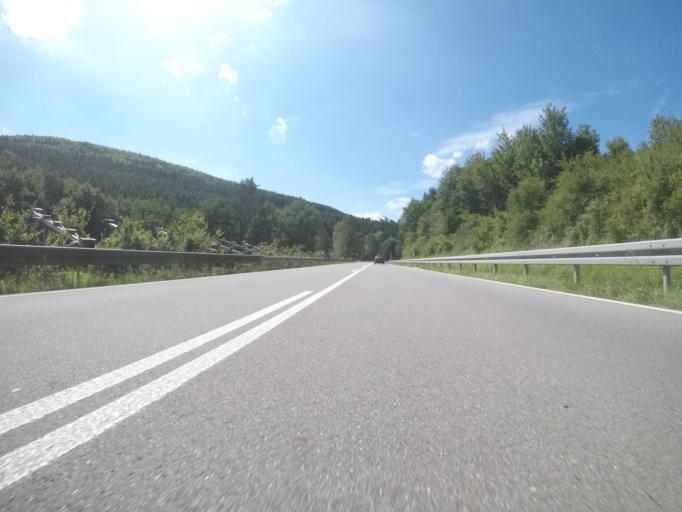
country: DE
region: Baden-Wuerttemberg
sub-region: Karlsruhe Region
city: Ebhausen
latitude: 48.5891
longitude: 8.6652
